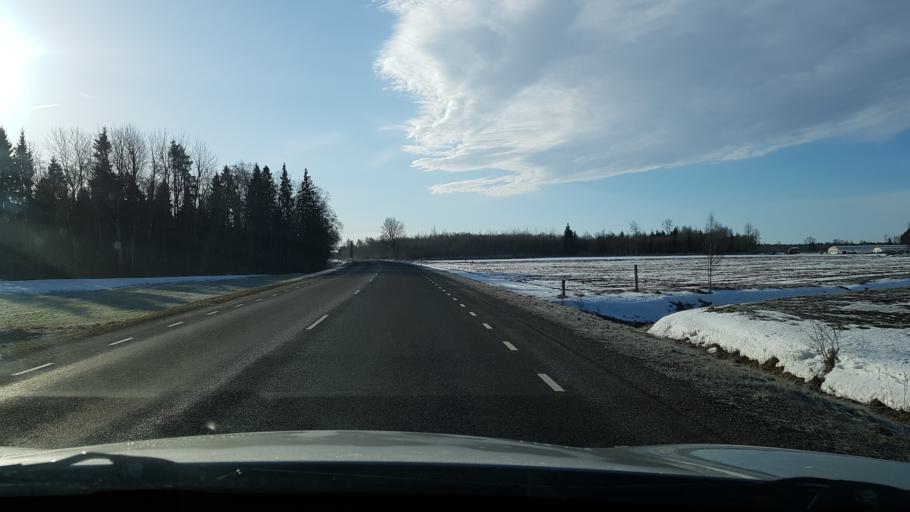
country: EE
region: Viljandimaa
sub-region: Vohma linn
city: Vohma
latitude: 58.6216
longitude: 25.5689
